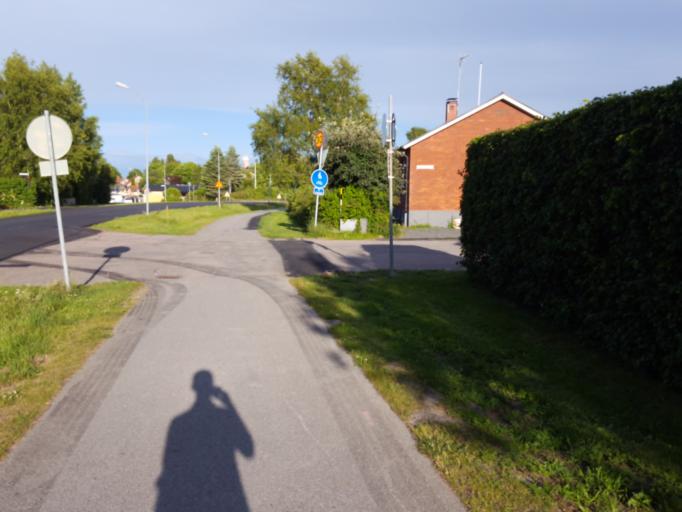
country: SE
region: Uppsala
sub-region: Osthammars Kommun
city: OEsthammar
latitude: 60.2606
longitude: 18.3538
